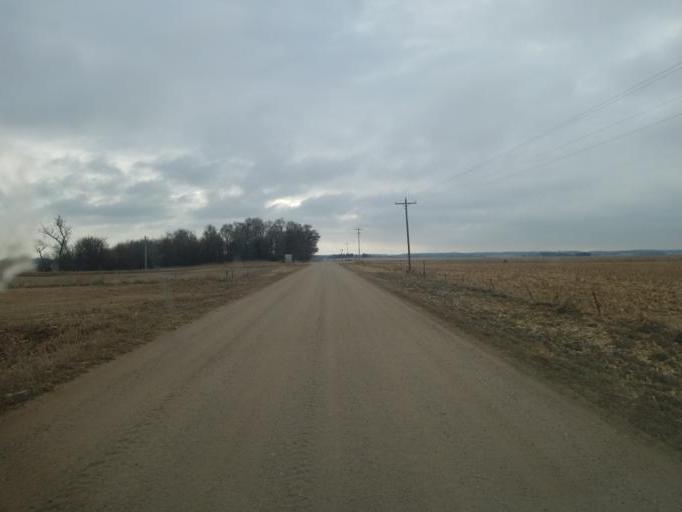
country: US
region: Nebraska
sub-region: Pierce County
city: Plainview
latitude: 42.3812
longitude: -97.7956
